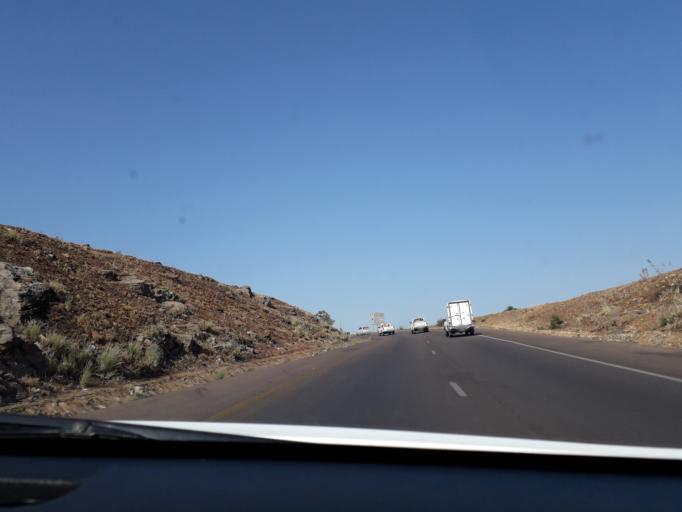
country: ZA
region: Gauteng
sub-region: City of Tshwane Metropolitan Municipality
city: Pretoria
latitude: -25.7857
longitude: 28.1917
